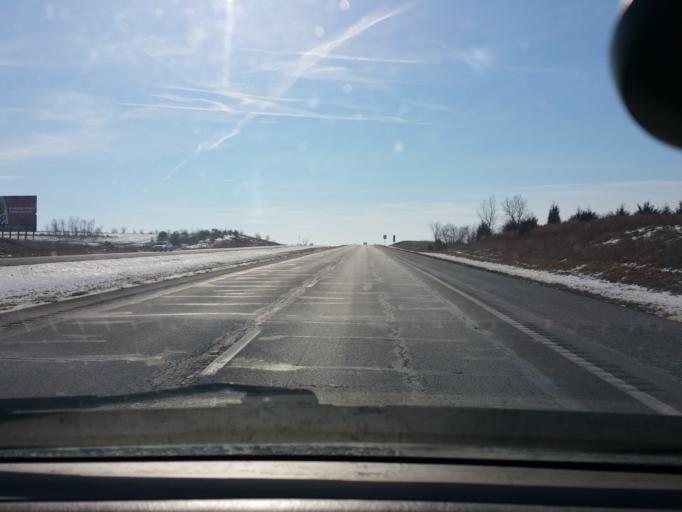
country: US
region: Missouri
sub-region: Harrison County
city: Bethany
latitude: 40.2027
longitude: -94.0141
